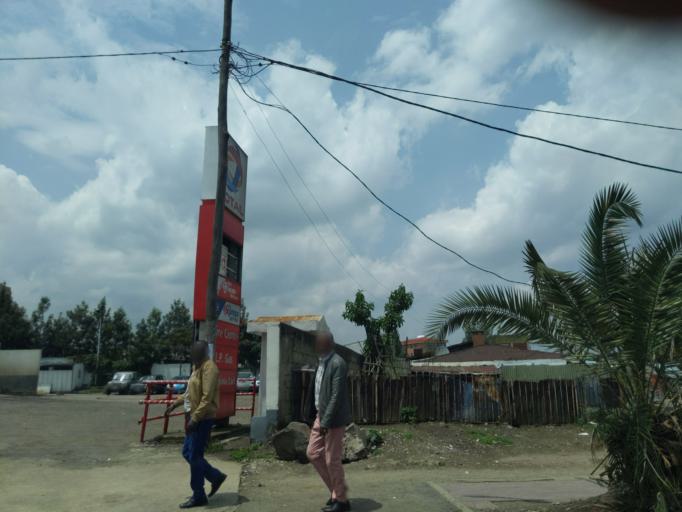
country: ET
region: Adis Abeba
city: Addis Ababa
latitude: 8.9592
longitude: 38.7640
